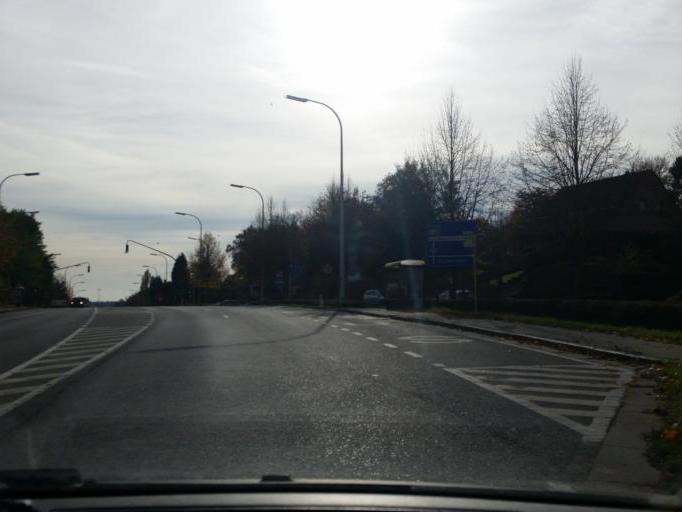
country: BE
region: Flanders
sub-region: Provincie Vlaams-Brabant
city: Grimbergen
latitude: 50.9220
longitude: 4.3649
